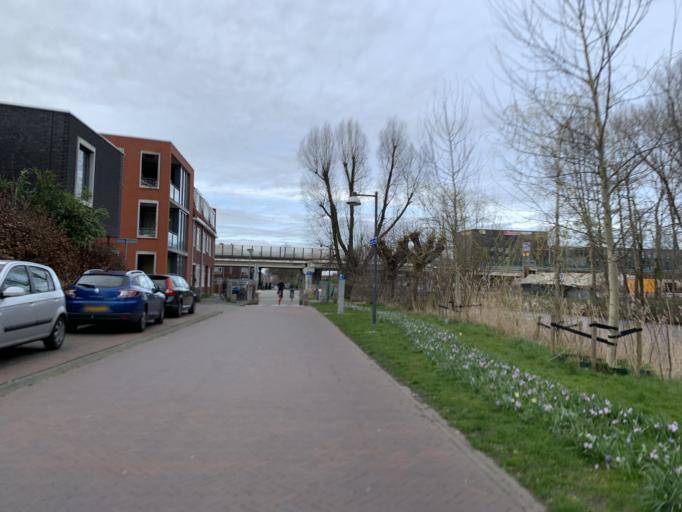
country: NL
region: Groningen
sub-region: Gemeente Groningen
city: Oosterpark
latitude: 53.2086
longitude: 6.5841
